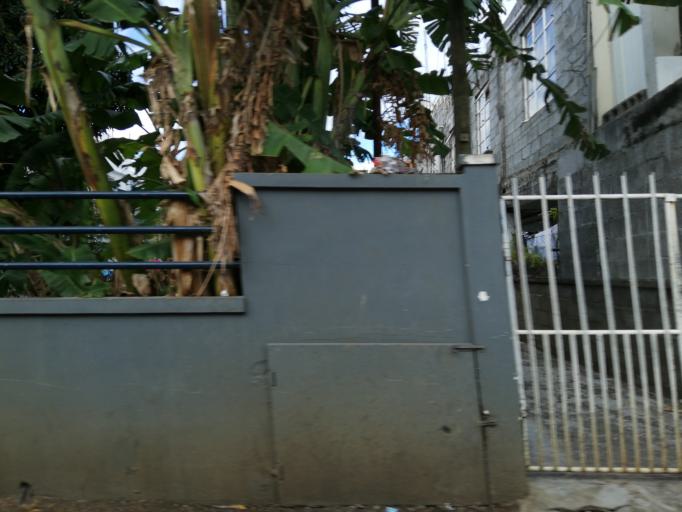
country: MU
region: Black River
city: Gros Cailloux
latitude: -20.2305
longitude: 57.4542
